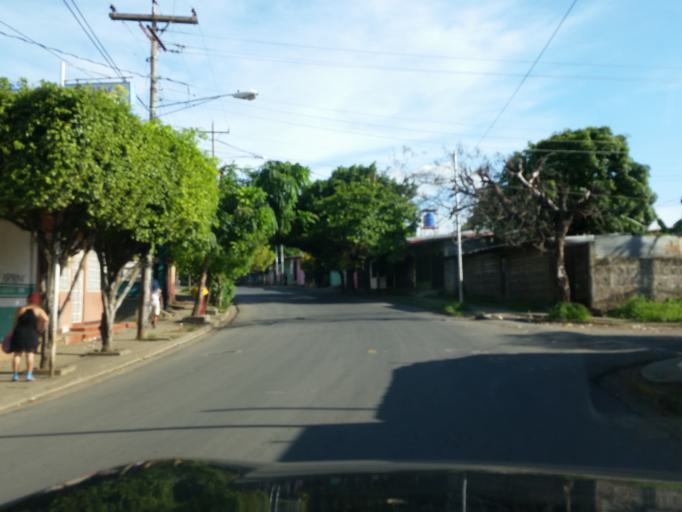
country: NI
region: Managua
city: Managua
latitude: 12.1076
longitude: -86.2237
